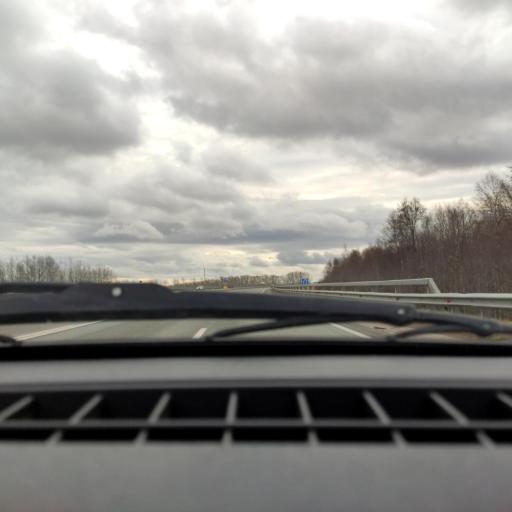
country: RU
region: Bashkortostan
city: Asanovo
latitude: 54.9656
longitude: 55.5829
